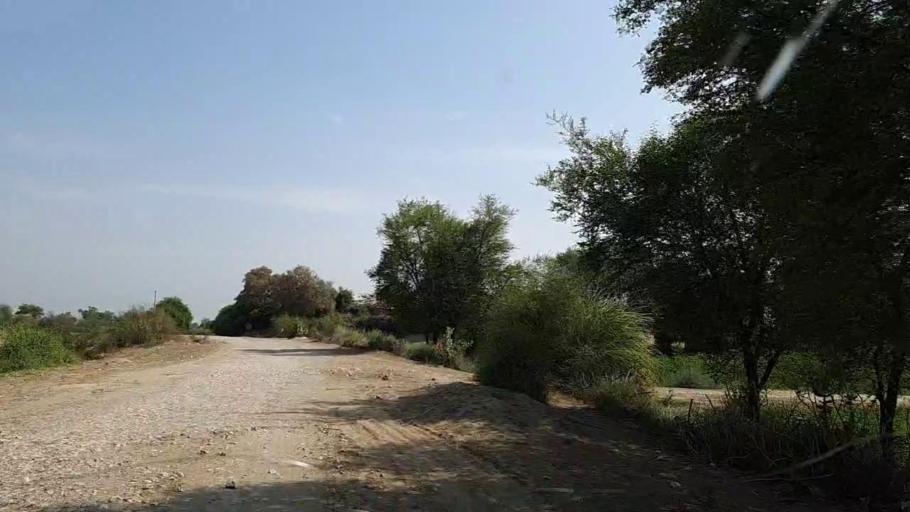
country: PK
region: Sindh
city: Khanpur
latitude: 27.7300
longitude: 69.3585
